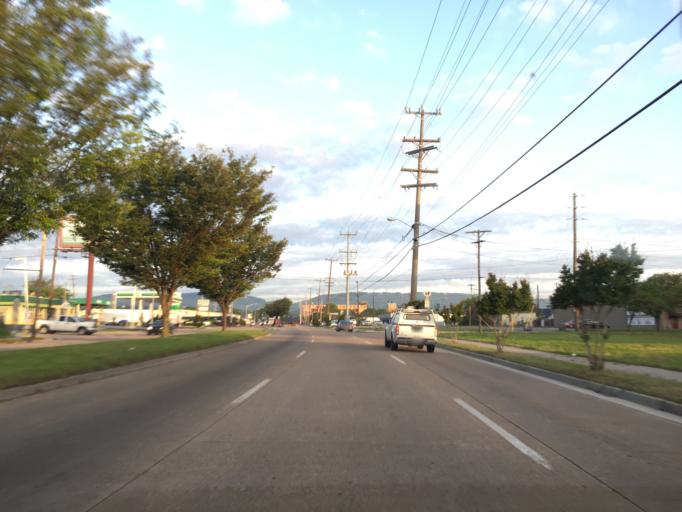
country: US
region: Tennessee
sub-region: Hamilton County
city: Chattanooga
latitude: 35.0322
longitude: -85.3101
